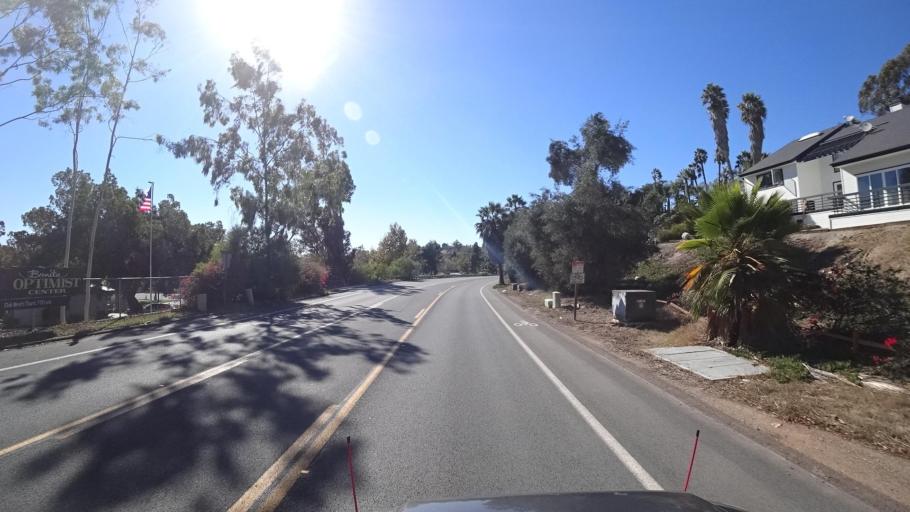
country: US
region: California
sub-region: San Diego County
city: Bonita
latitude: 32.6655
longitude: -117.0352
